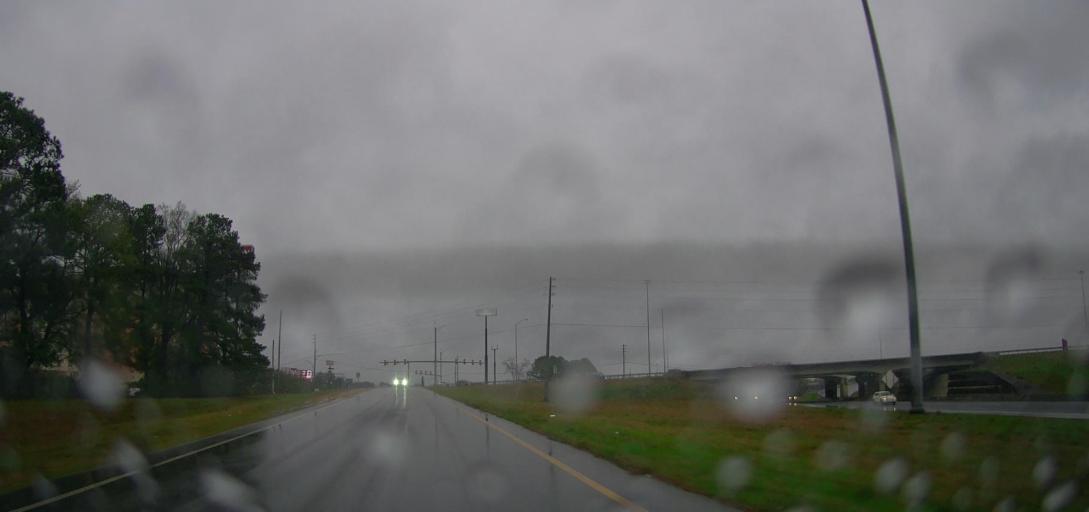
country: US
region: Alabama
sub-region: Montgomery County
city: Montgomery
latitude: 32.3642
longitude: -86.2154
